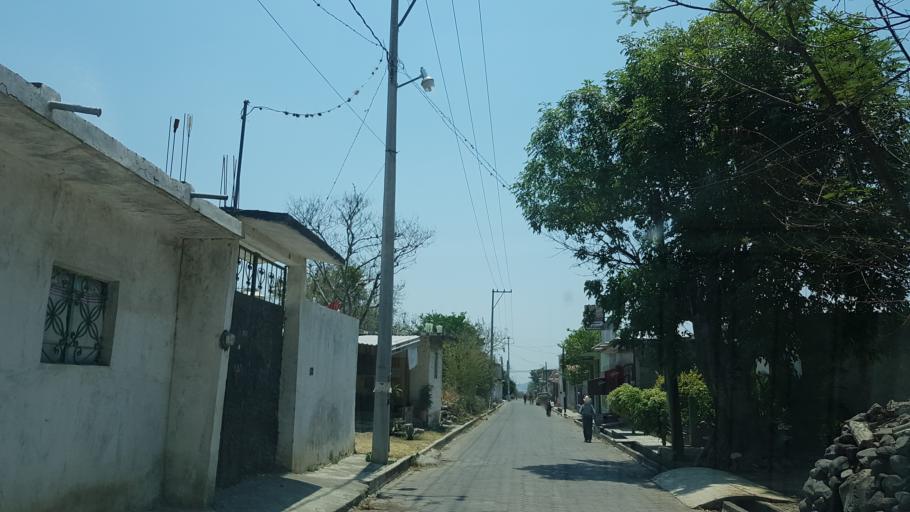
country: MX
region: Puebla
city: Huaquechula
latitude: 18.7725
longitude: -98.5458
